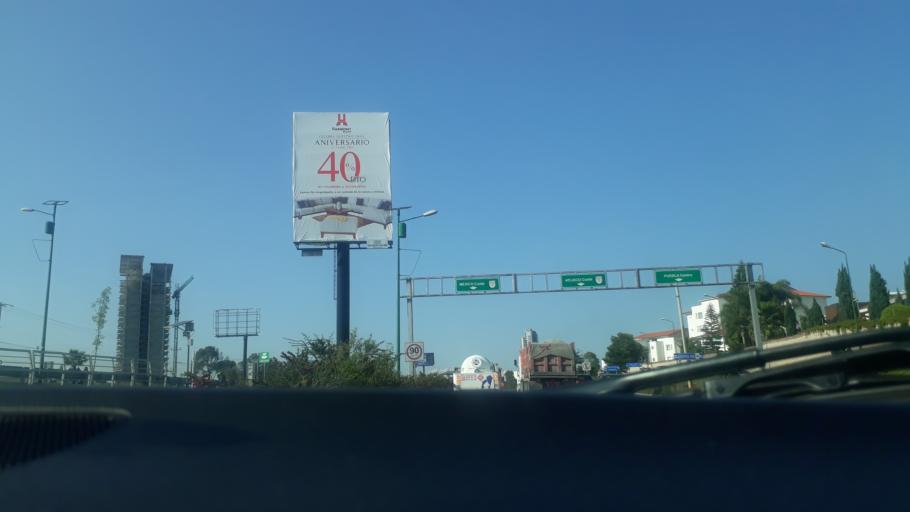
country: MX
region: Puebla
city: Tlazcalancingo
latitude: 19.0032
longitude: -98.2603
